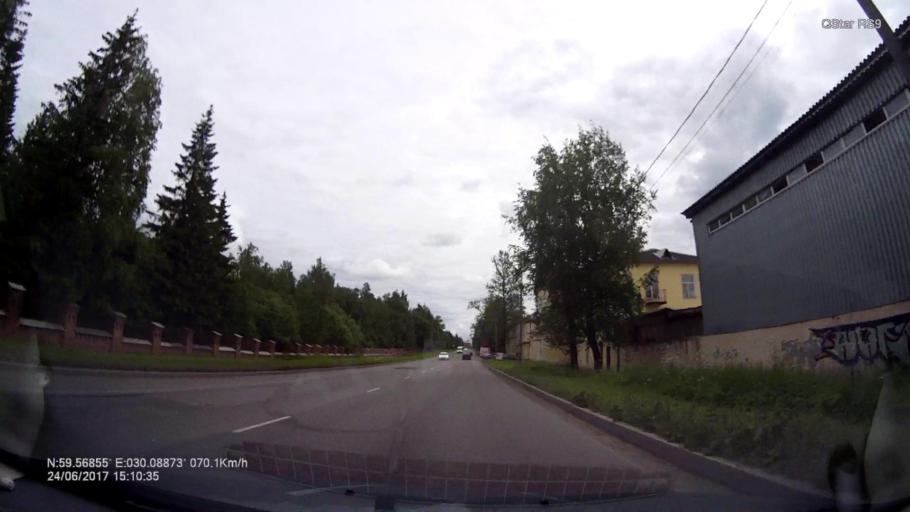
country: RU
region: Leningrad
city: Mariyenburg
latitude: 59.5684
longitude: 30.0890
